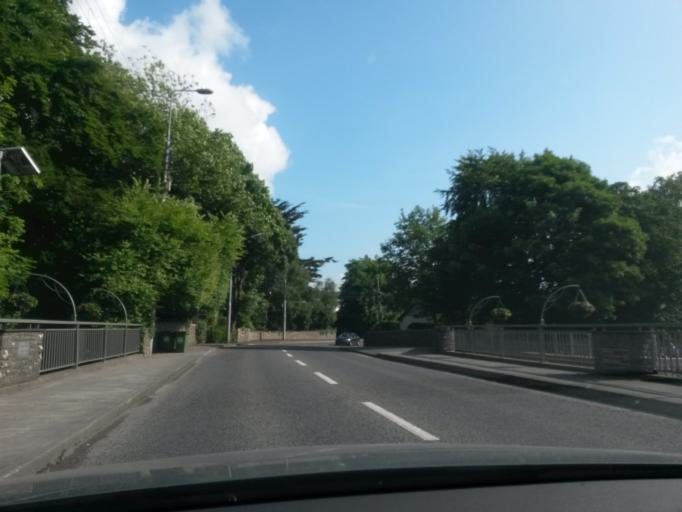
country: IE
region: Munster
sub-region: An Clar
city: Ennis
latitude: 52.8482
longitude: -8.9725
